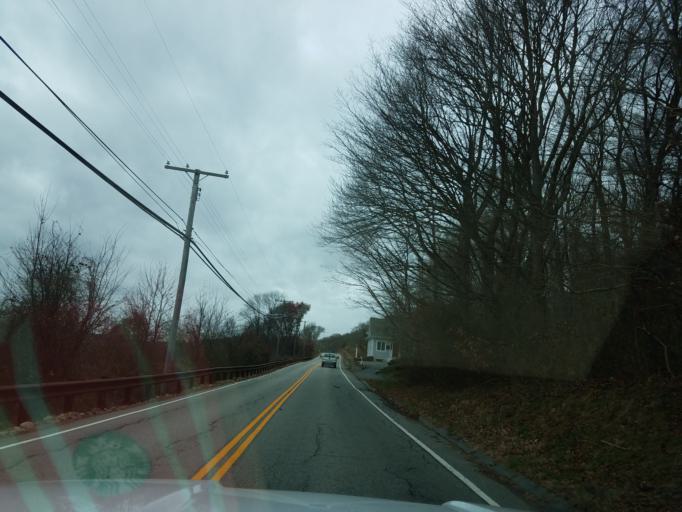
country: US
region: Connecticut
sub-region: New London County
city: Conning Towers-Nautilus Park
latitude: 41.3792
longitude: -72.0875
